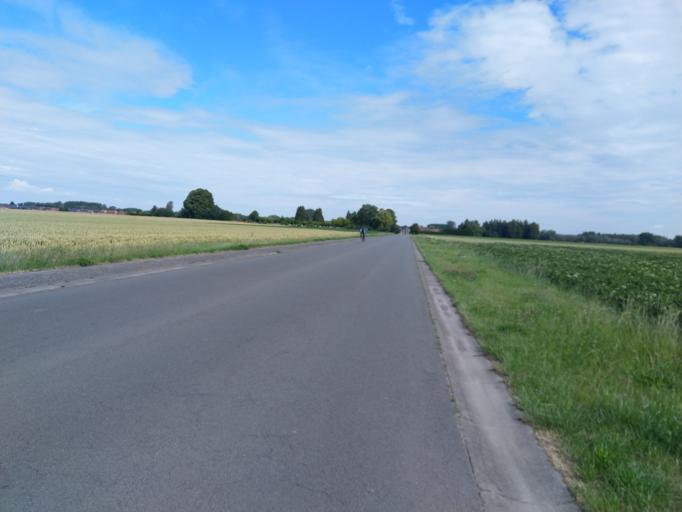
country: BE
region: Wallonia
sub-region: Province du Hainaut
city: Quievrain
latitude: 50.4195
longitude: 3.6952
